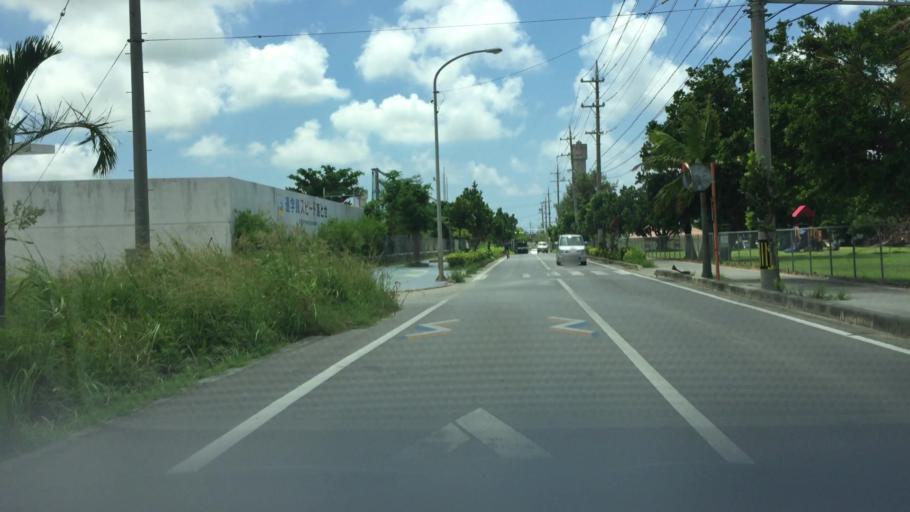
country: JP
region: Okinawa
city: Ishigaki
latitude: 24.3557
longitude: 124.1363
